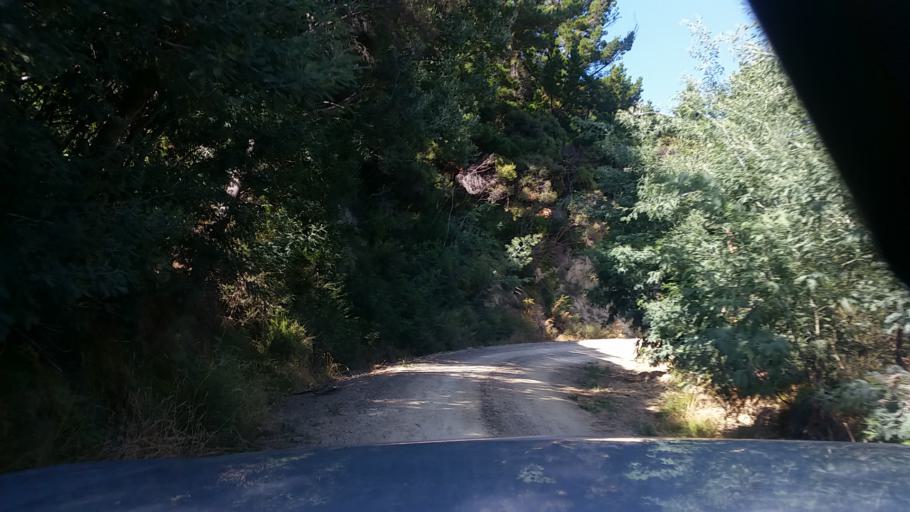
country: NZ
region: Marlborough
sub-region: Marlborough District
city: Picton
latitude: -41.3052
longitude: 174.1761
